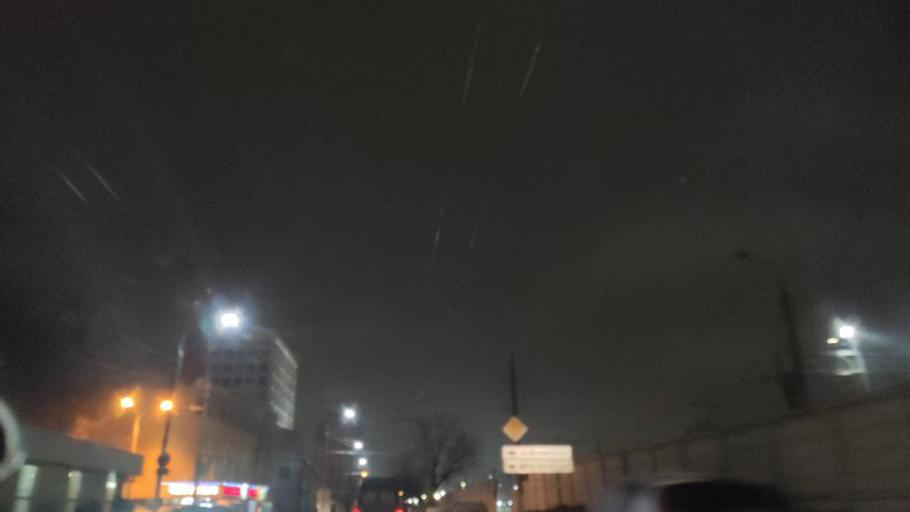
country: RU
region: Moskovskaya
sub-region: Podol'skiy Rayon
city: Podol'sk
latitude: 55.4312
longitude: 37.5662
